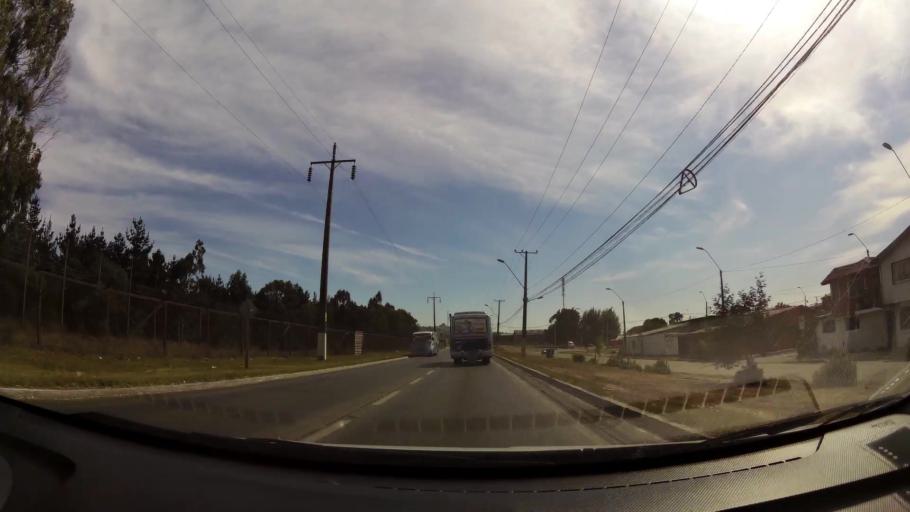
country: CL
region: Biobio
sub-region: Provincia de Concepcion
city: Talcahuano
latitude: -36.7318
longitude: -73.1186
